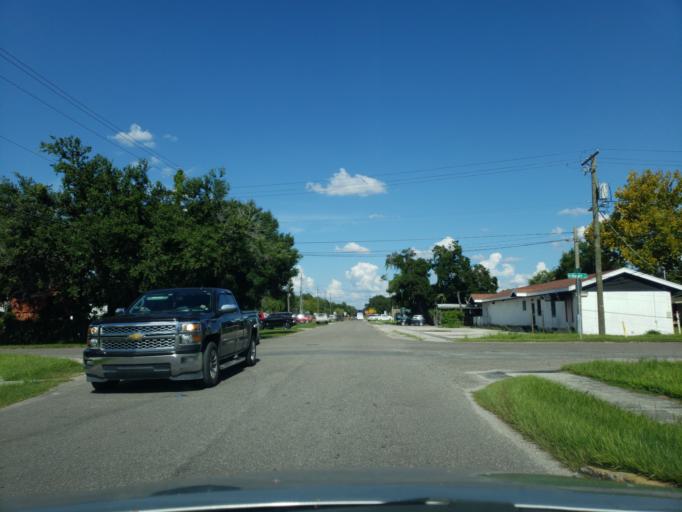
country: US
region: Florida
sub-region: Hillsborough County
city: Egypt Lake-Leto
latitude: 27.9865
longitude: -82.5159
